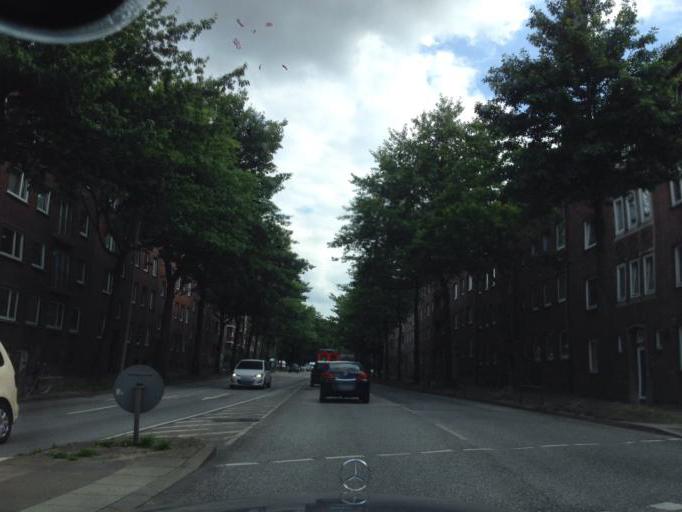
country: DE
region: Hamburg
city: Marienthal
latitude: 53.5507
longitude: 10.0847
